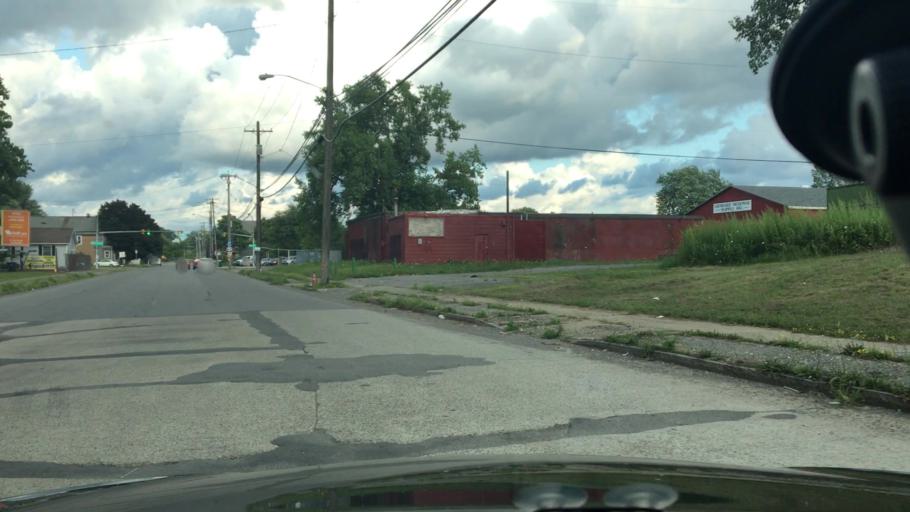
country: US
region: New York
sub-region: Erie County
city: West Seneca
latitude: 42.8651
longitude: -78.8272
